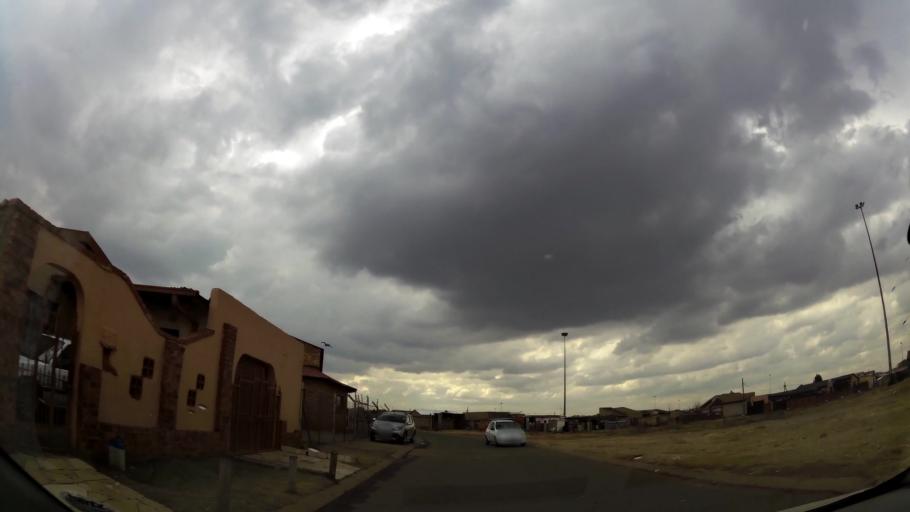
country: ZA
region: Gauteng
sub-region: Ekurhuleni Metropolitan Municipality
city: Germiston
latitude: -26.3674
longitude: 28.1602
